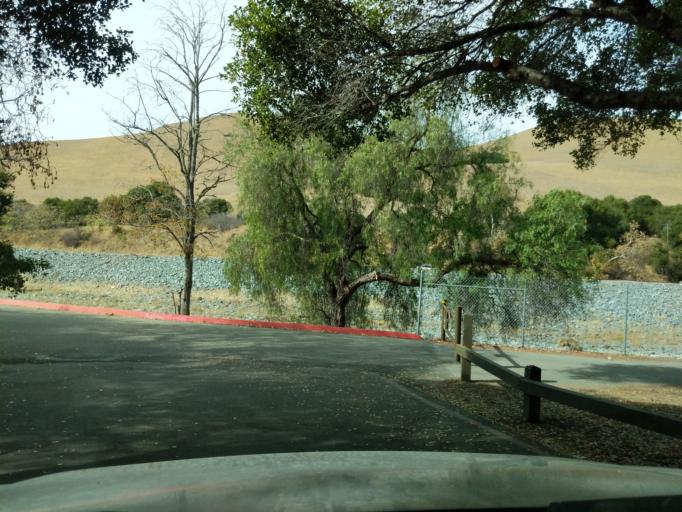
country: US
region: California
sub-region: Alameda County
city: Fremont
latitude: 37.5796
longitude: -121.9656
